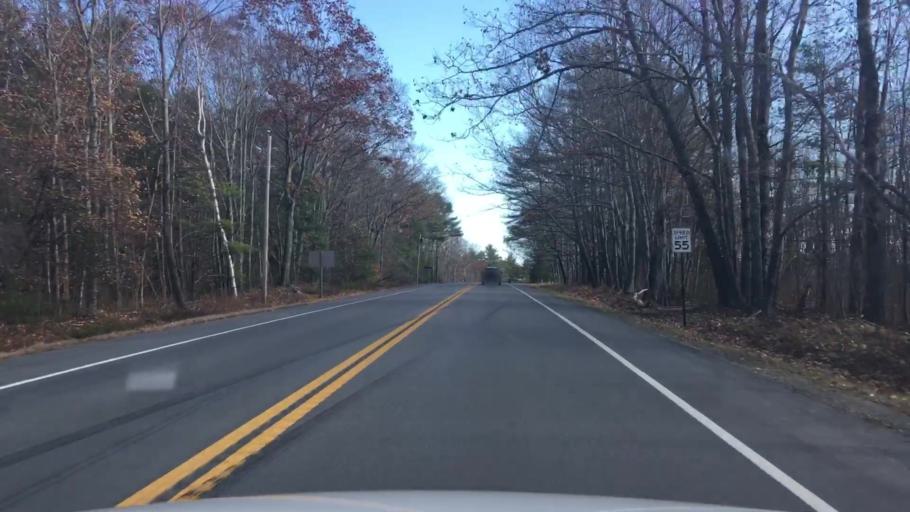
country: US
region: Maine
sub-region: Lincoln County
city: Jefferson
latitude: 44.2560
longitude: -69.4434
